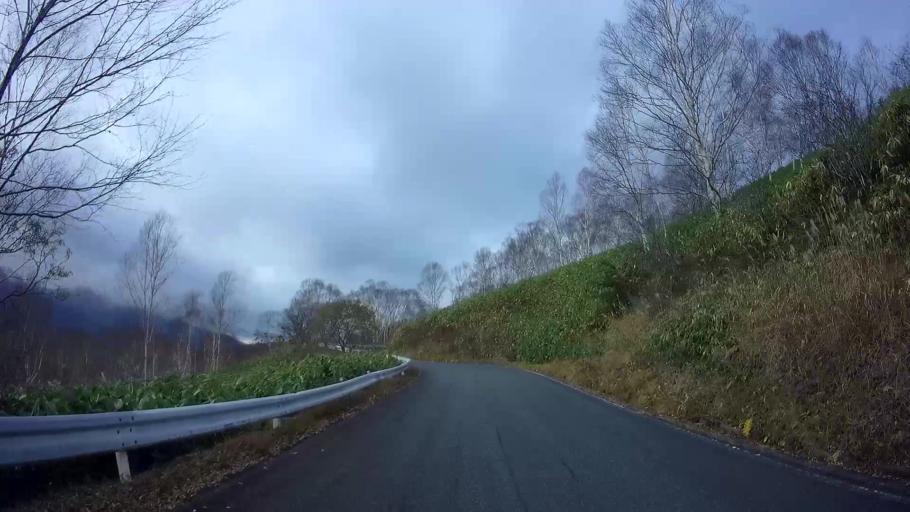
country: JP
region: Gunma
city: Nakanojomachi
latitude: 36.7138
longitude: 138.6514
